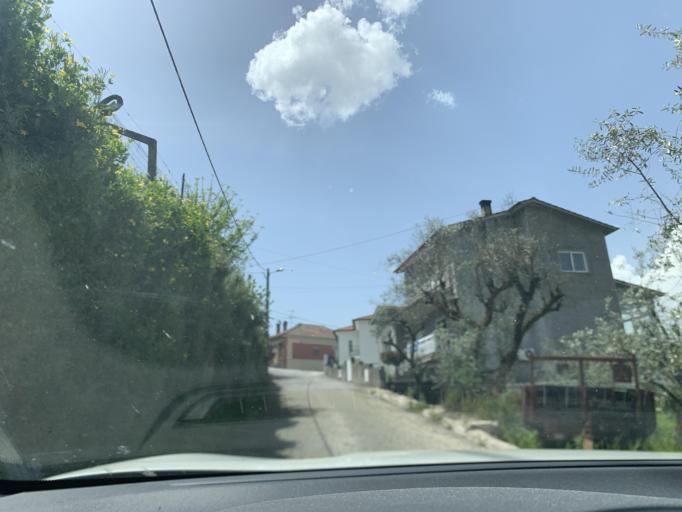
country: PT
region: Viseu
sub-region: Mangualde
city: Mangualde
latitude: 40.6083
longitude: -7.7727
